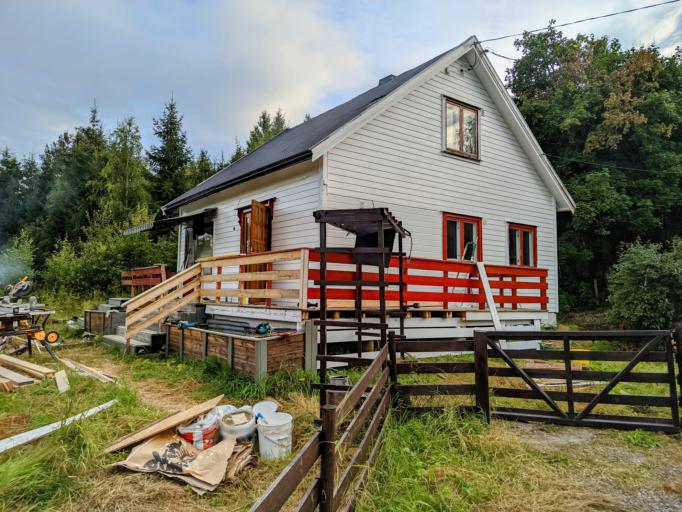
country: NO
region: Hedmark
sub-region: Grue
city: Kirkenaer
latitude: 60.4196
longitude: 11.9957
